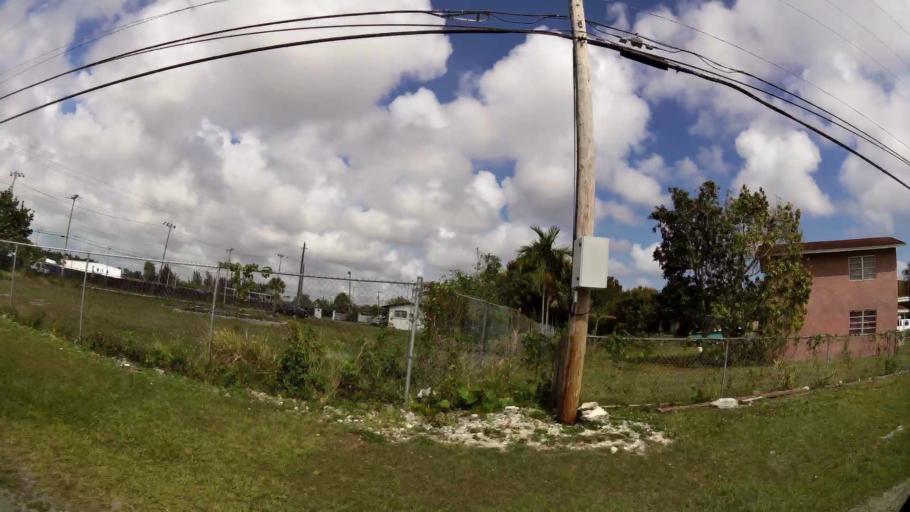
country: BS
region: Freeport
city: Freeport
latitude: 26.5386
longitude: -78.6928
